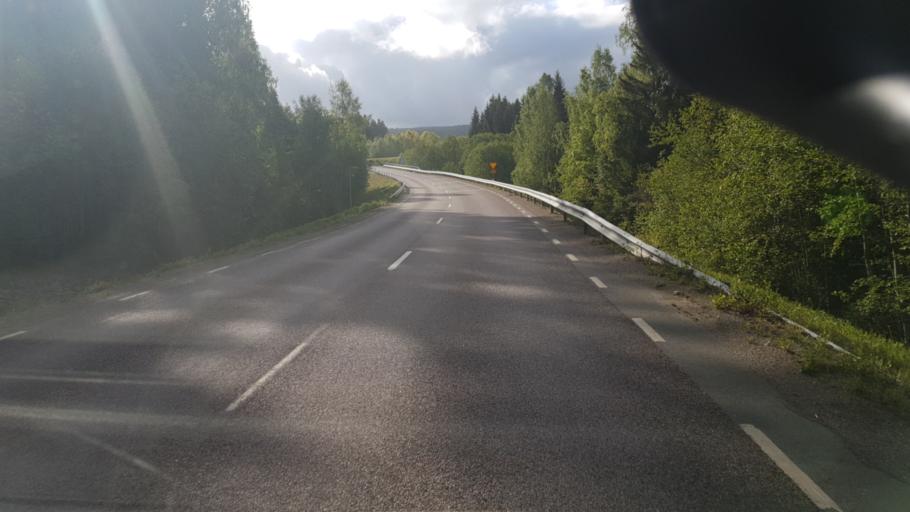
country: SE
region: Vaermland
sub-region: Eda Kommun
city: Amotfors
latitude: 59.7294
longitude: 12.1777
